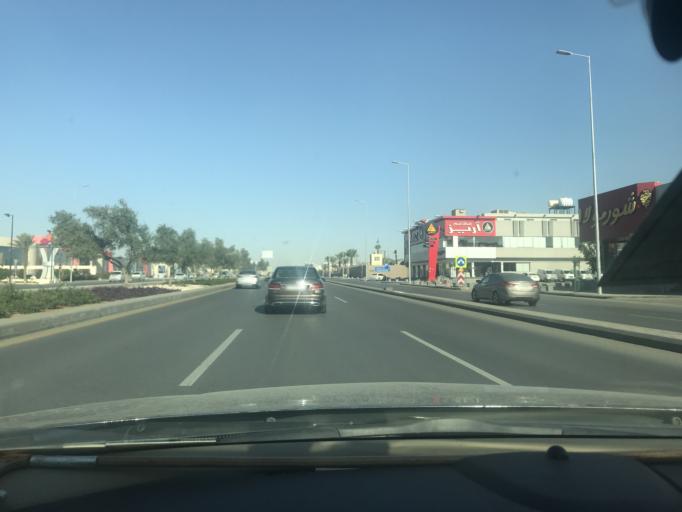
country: SA
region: Ar Riyad
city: Riyadh
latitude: 24.7407
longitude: 46.6833
